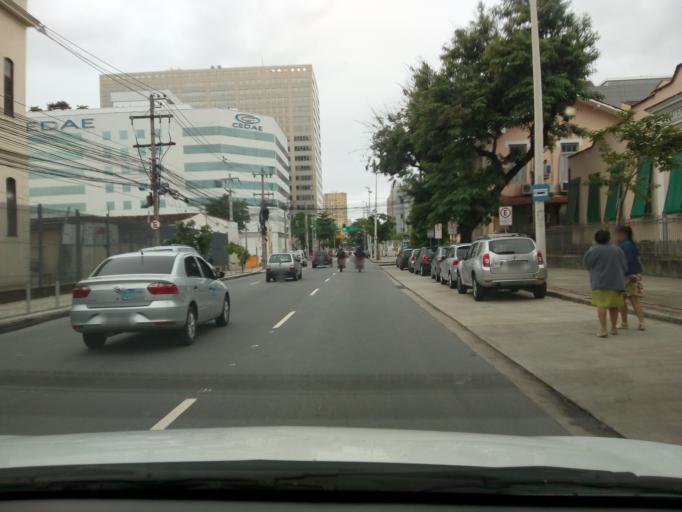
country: BR
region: Rio de Janeiro
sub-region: Rio De Janeiro
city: Rio de Janeiro
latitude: -22.9097
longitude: -43.2015
